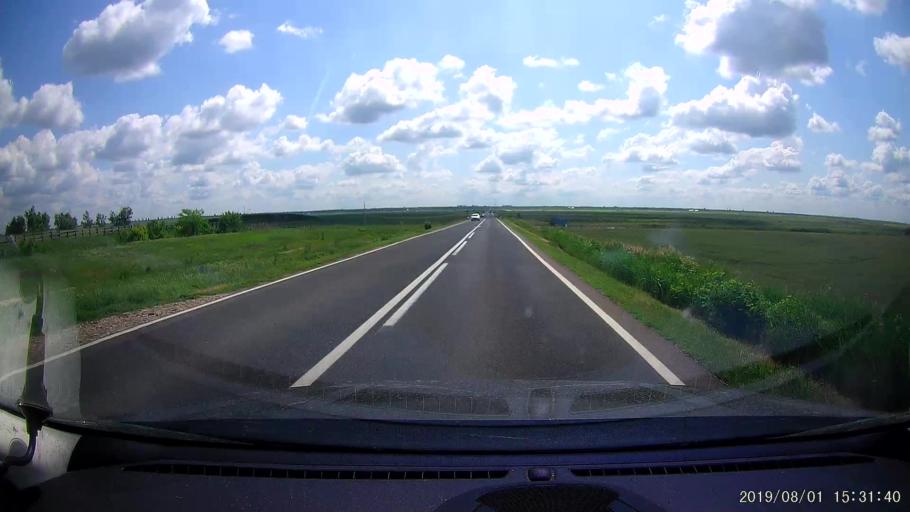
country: RO
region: Braila
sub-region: Comuna Insuratei
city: Insuratei
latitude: 44.9422
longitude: 27.6551
